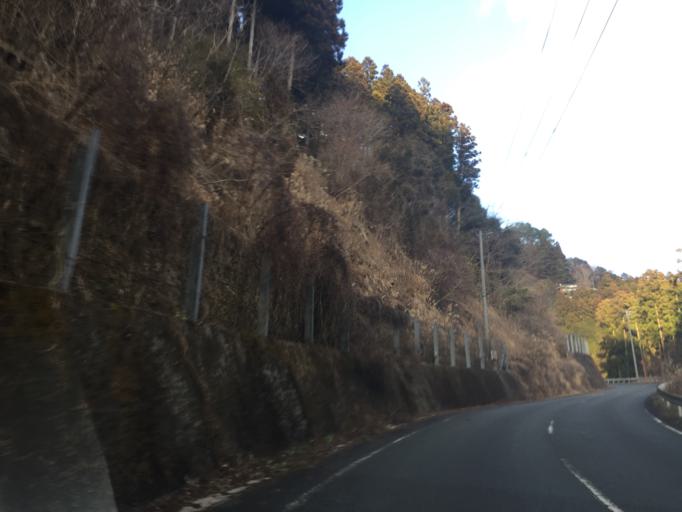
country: JP
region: Shizuoka
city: Mori
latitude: 34.8984
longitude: 137.9823
